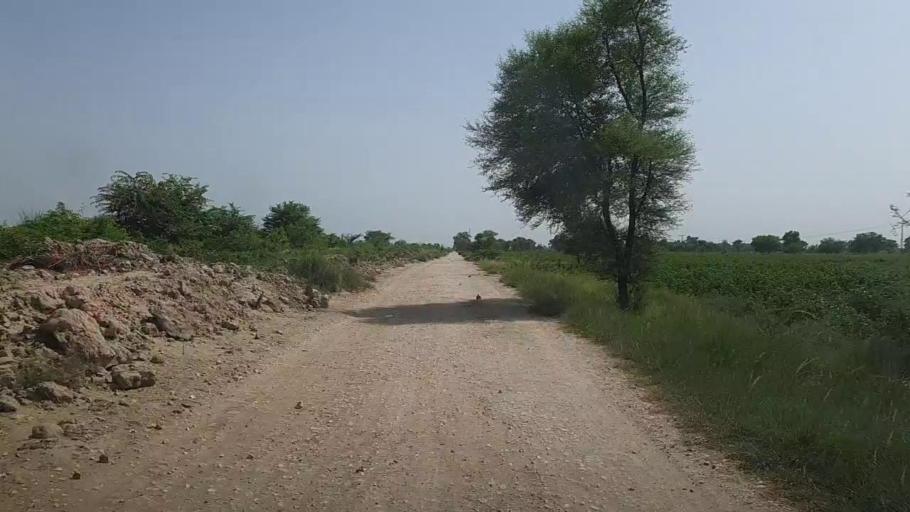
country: PK
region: Sindh
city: Pad Idan
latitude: 26.7916
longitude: 68.3279
